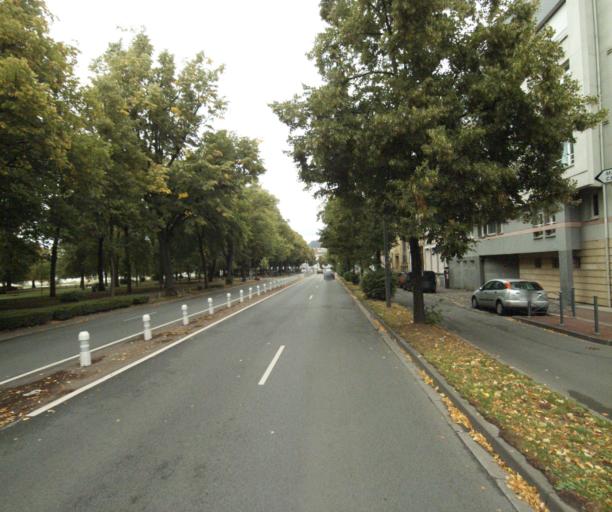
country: FR
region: Nord-Pas-de-Calais
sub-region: Departement du Nord
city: Lille
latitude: 50.6411
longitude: 3.0536
